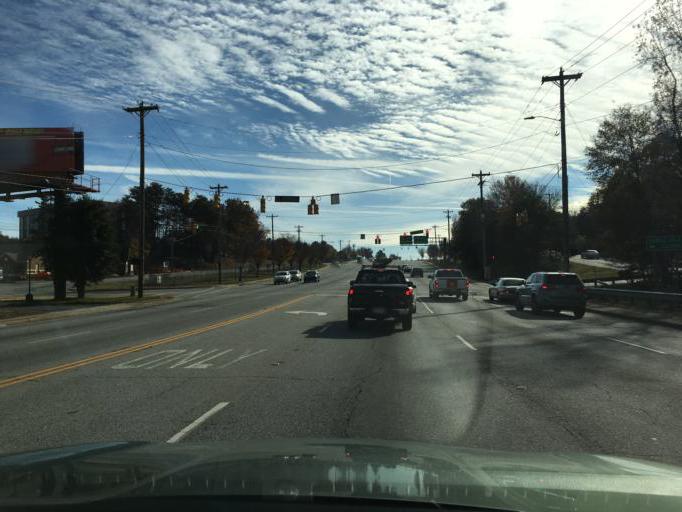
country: US
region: South Carolina
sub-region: Greenville County
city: Greenville
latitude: 34.8623
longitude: -82.3570
